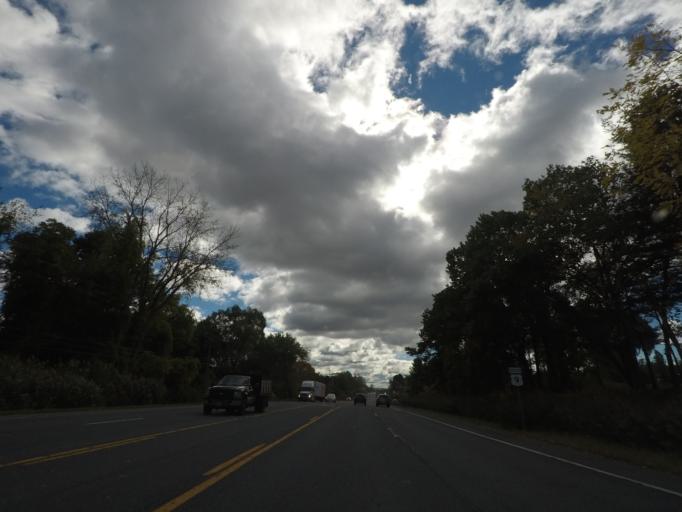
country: US
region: New York
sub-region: Saratoga County
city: Waterford
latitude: 42.8319
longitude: -73.7373
